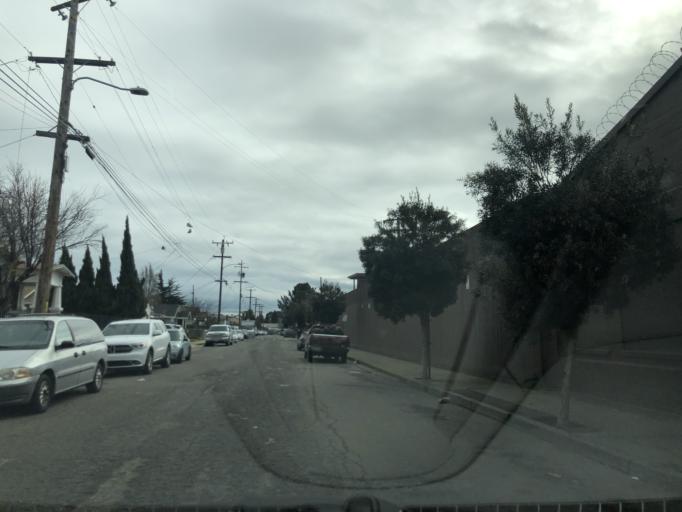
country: US
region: California
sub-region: Alameda County
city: San Leandro
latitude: 37.7343
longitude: -122.1763
